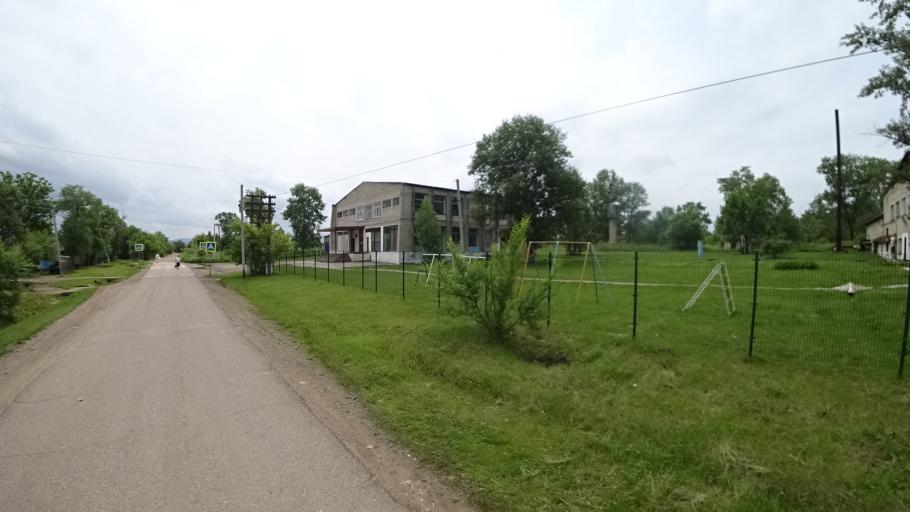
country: RU
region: Primorskiy
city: Novosysoyevka
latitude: 44.2392
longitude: 133.3640
